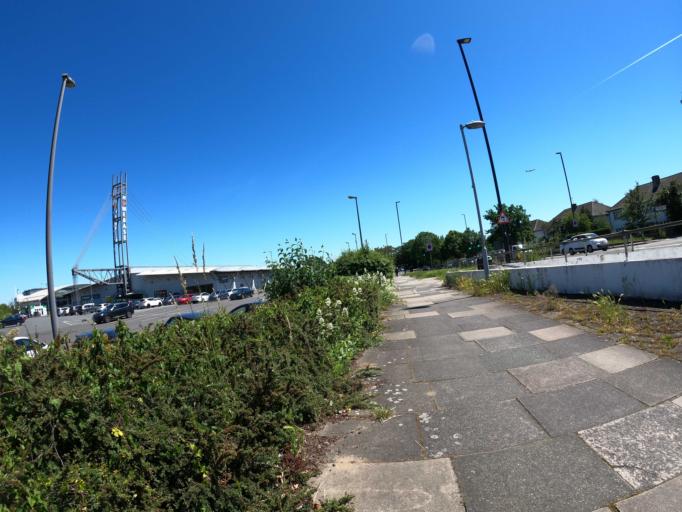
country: GB
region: England
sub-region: Greater London
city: Isleworth
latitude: 51.4831
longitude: -0.3264
